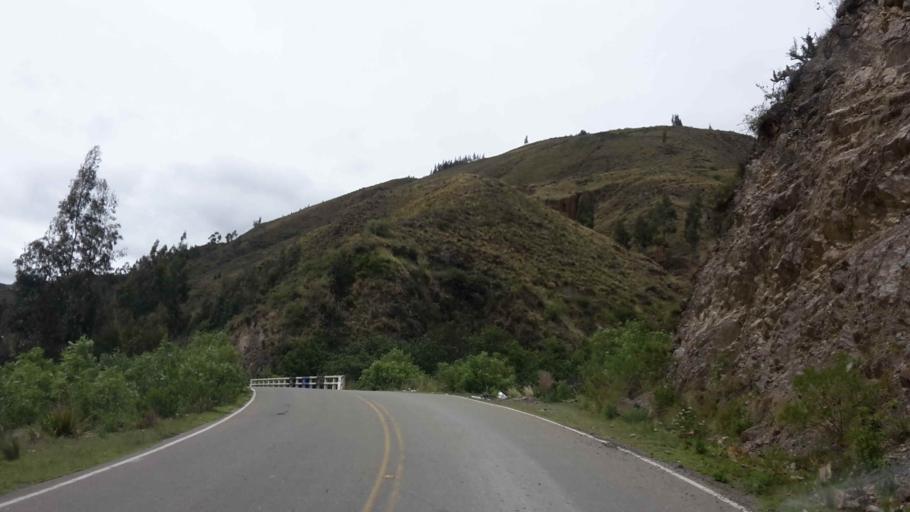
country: BO
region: Cochabamba
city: Colomi
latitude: -17.4049
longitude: -65.7895
